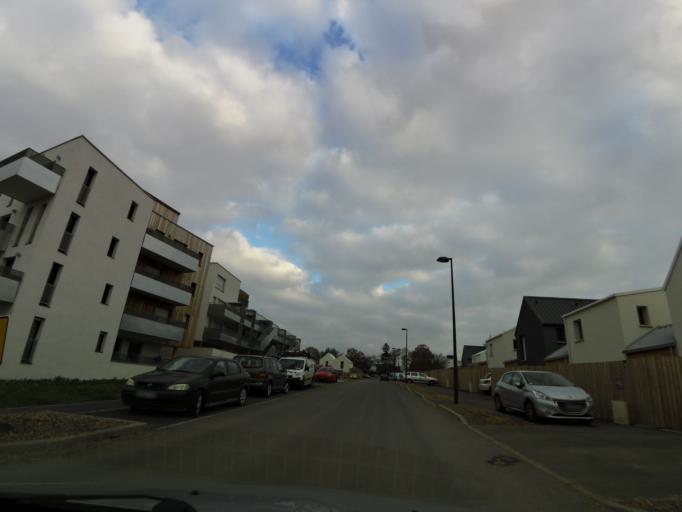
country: FR
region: Brittany
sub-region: Departement d'Ille-et-Vilaine
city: Orgeres
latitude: 47.9954
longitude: -1.6721
